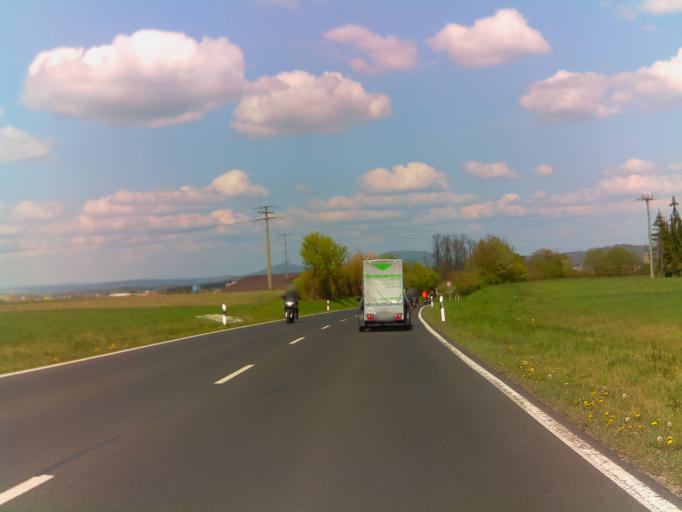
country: DE
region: Bavaria
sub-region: Regierungsbezirk Unterfranken
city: Bad Konigshofen im Grabfeld
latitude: 50.2887
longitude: 10.4424
